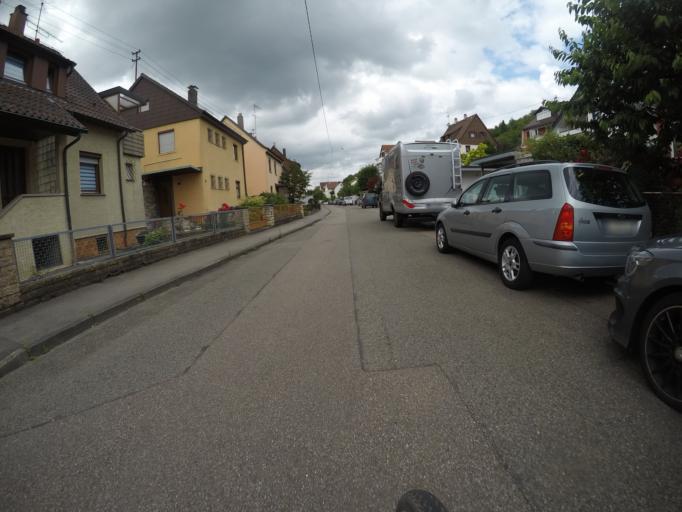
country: DE
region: Baden-Wuerttemberg
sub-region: Regierungsbezirk Stuttgart
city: Altbach
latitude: 48.7262
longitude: 9.3568
